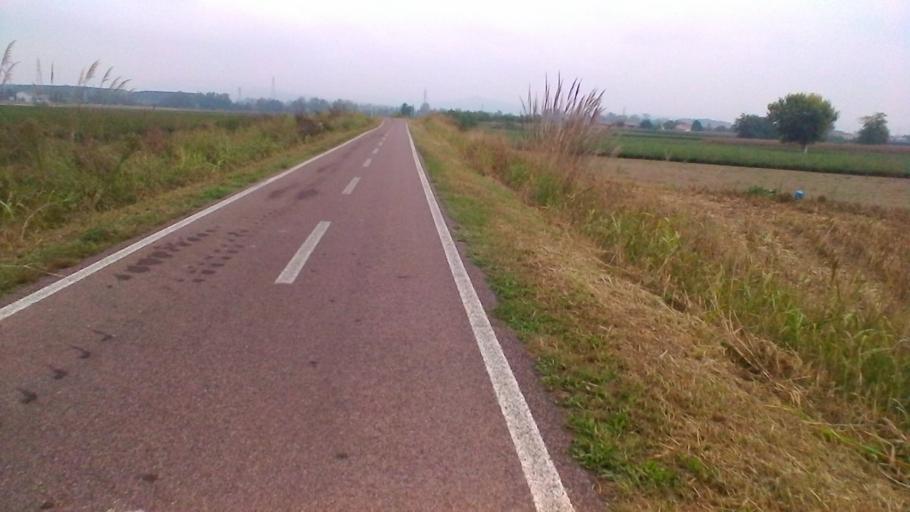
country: IT
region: Veneto
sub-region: Provincia di Verona
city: Campagnola
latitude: 45.3869
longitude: 11.0714
